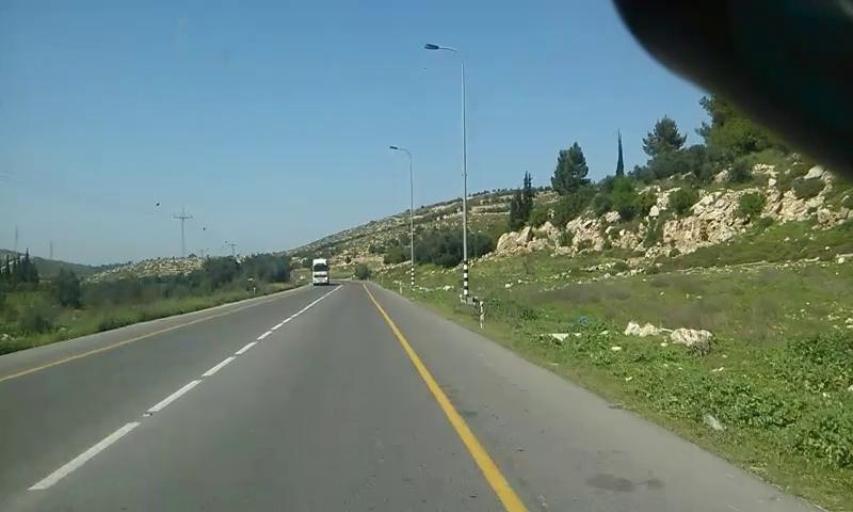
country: PS
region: West Bank
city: Idhna
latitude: 31.5774
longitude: 34.9797
